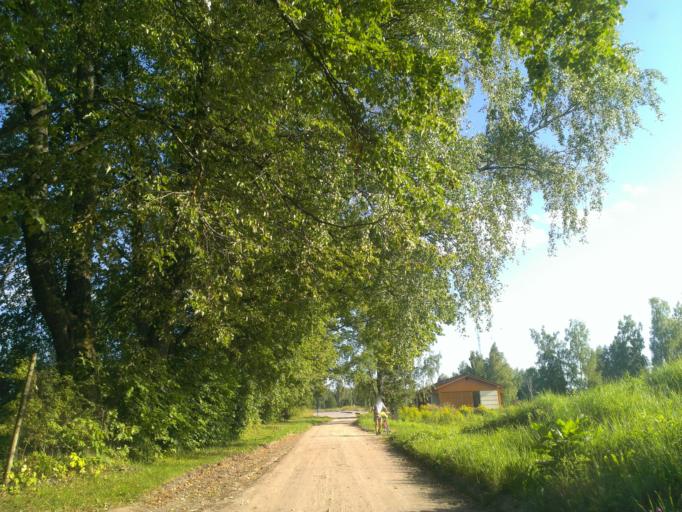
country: LV
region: Sigulda
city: Sigulda
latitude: 57.1683
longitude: 24.8759
